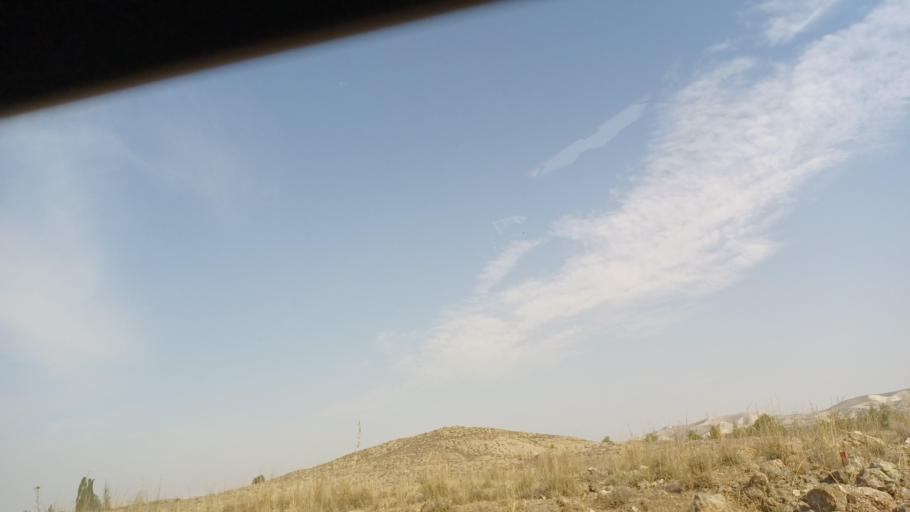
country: CY
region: Larnaka
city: Mosfiloti
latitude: 34.9656
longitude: 33.4407
